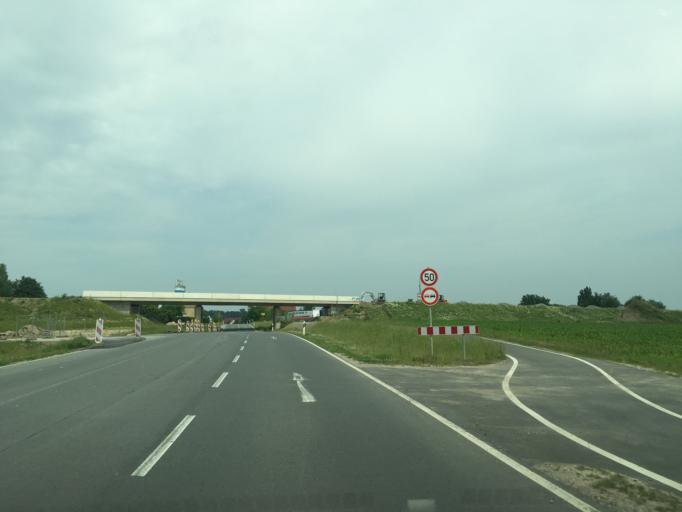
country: DE
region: North Rhine-Westphalia
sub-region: Regierungsbezirk Munster
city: Nordwalde
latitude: 52.0753
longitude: 7.4791
